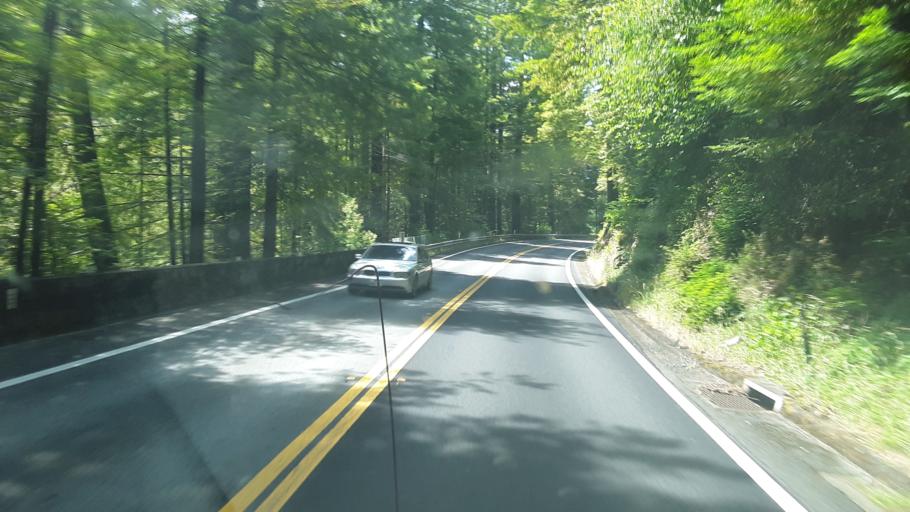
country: US
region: California
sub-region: Del Norte County
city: Bertsch-Oceanview
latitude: 41.8041
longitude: -124.0524
